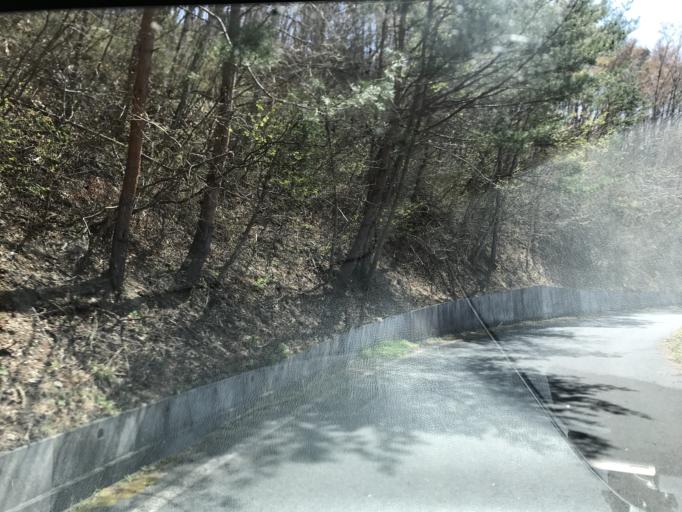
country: JP
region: Iwate
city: Ichinoseki
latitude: 38.8323
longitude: 141.2839
